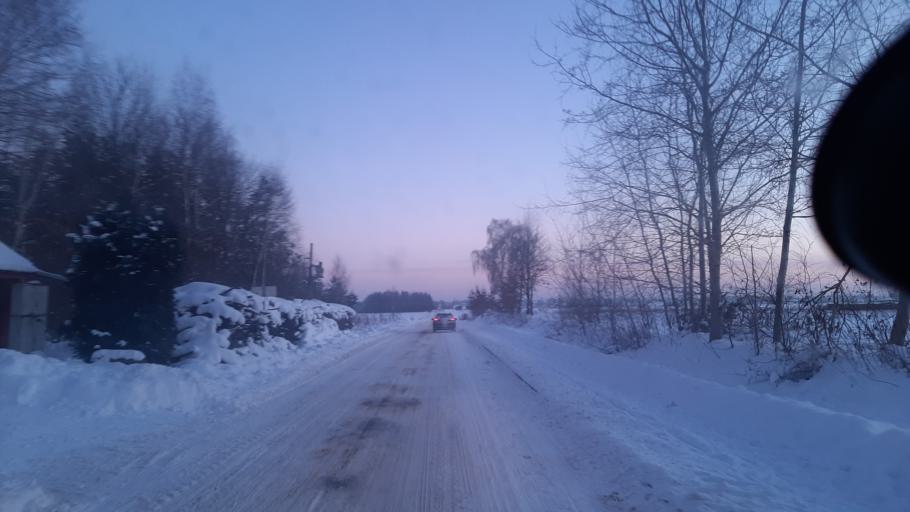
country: PL
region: Lublin Voivodeship
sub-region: Powiat lubelski
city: Jastkow
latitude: 51.3703
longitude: 22.5233
